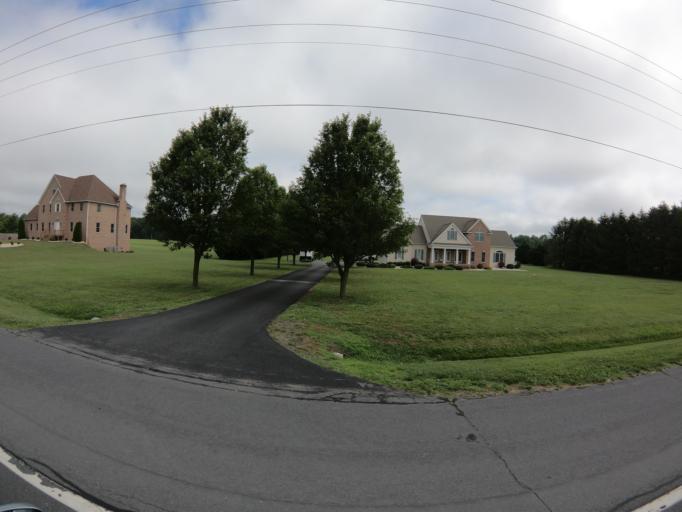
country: US
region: Delaware
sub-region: Kent County
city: Felton
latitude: 39.0056
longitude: -75.5417
